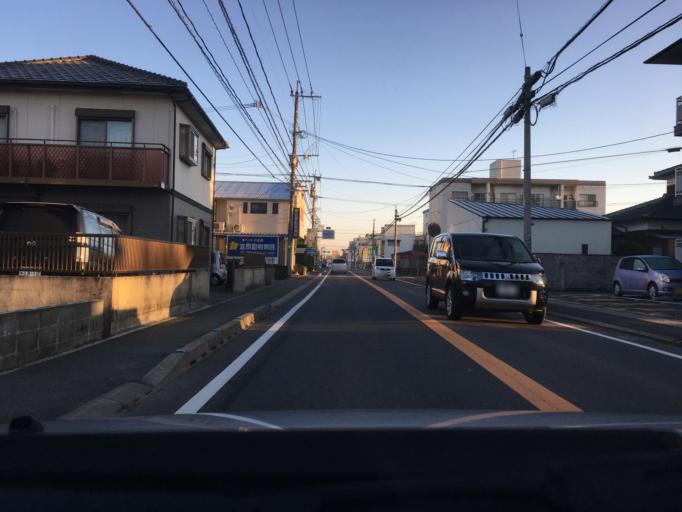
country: JP
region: Fukuoka
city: Kurume
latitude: 33.2962
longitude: 130.4965
